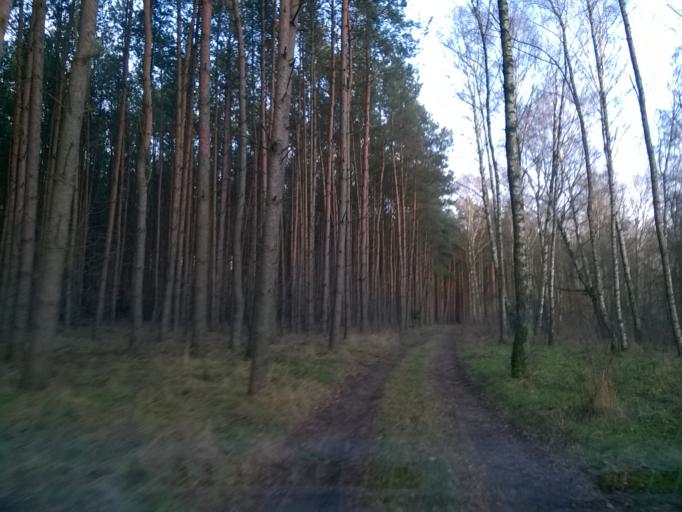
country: PL
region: Kujawsko-Pomorskie
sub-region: Powiat nakielski
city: Kcynia
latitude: 53.0260
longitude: 17.4408
